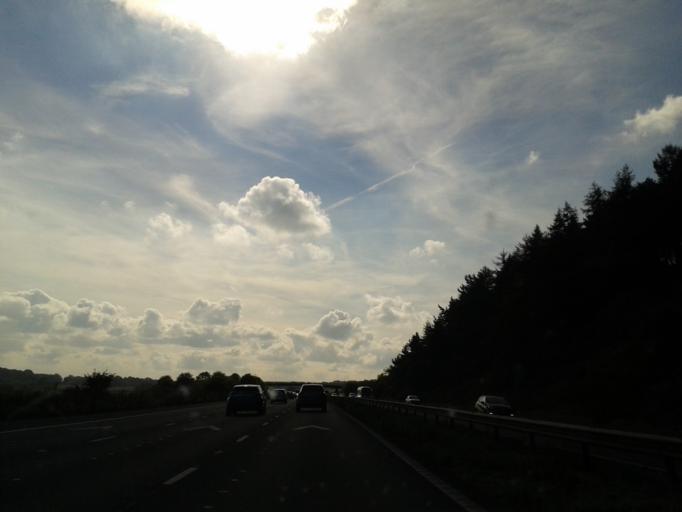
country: GB
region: England
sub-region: Staffordshire
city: Barlaston
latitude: 52.9384
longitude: -2.2153
